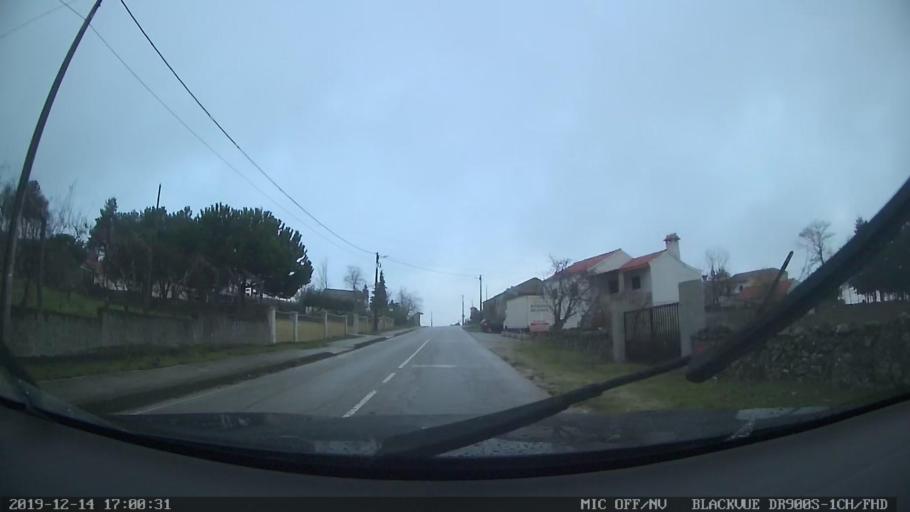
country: PT
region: Vila Real
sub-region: Vila Pouca de Aguiar
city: Vila Pouca de Aguiar
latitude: 41.4410
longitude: -7.5714
